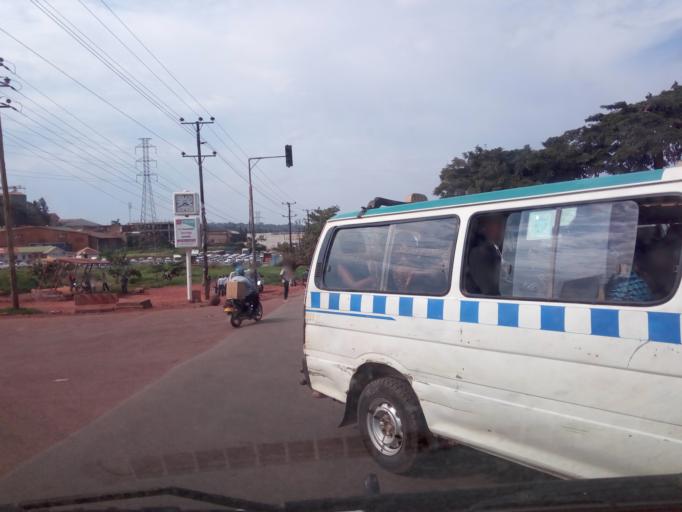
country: UG
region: Central Region
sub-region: Wakiso District
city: Kireka
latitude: 0.3337
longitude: 32.6179
